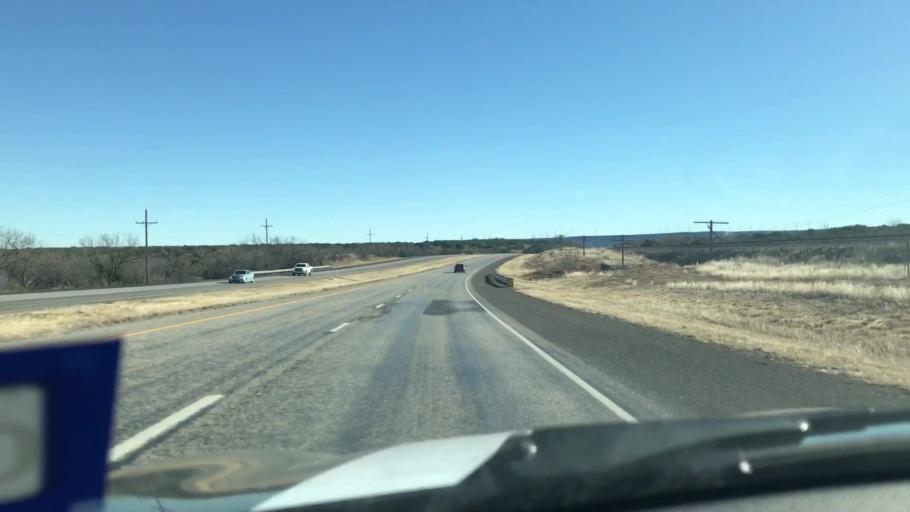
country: US
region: Texas
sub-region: Garza County
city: Post
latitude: 33.0283
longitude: -101.1867
